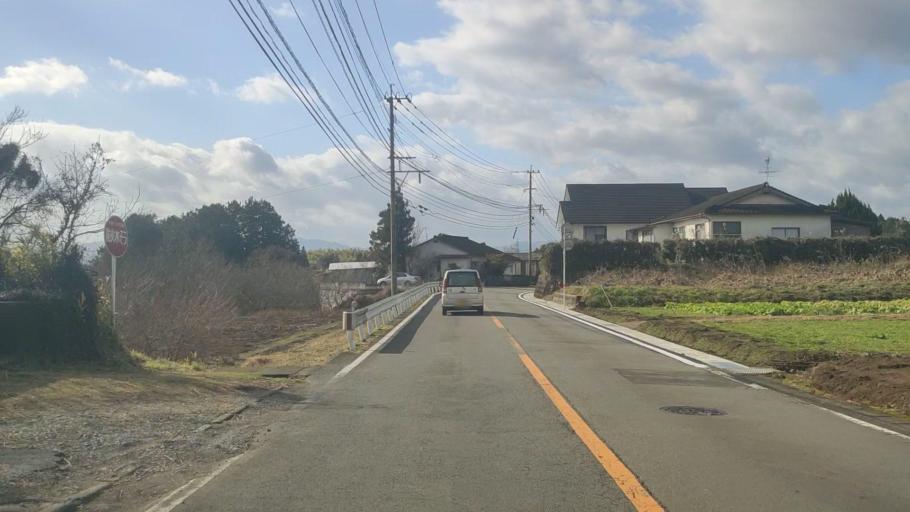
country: JP
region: Kumamoto
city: Hitoyoshi
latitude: 32.2331
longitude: 130.7878
